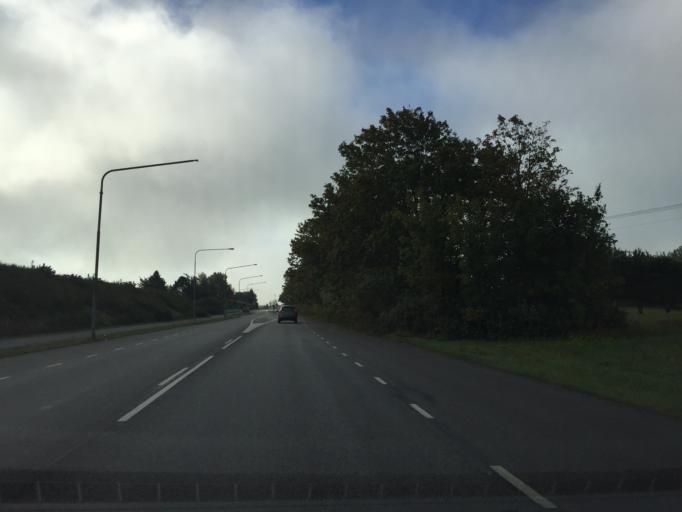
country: SE
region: Skane
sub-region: Staffanstorps Kommun
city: Staffanstorp
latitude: 55.6356
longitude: 13.1864
